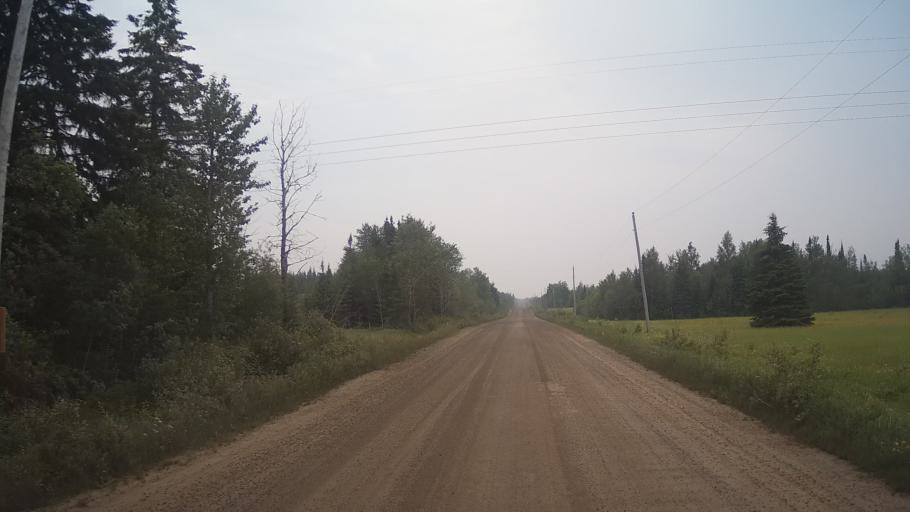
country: CA
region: Ontario
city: Hearst
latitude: 49.6420
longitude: -83.2783
